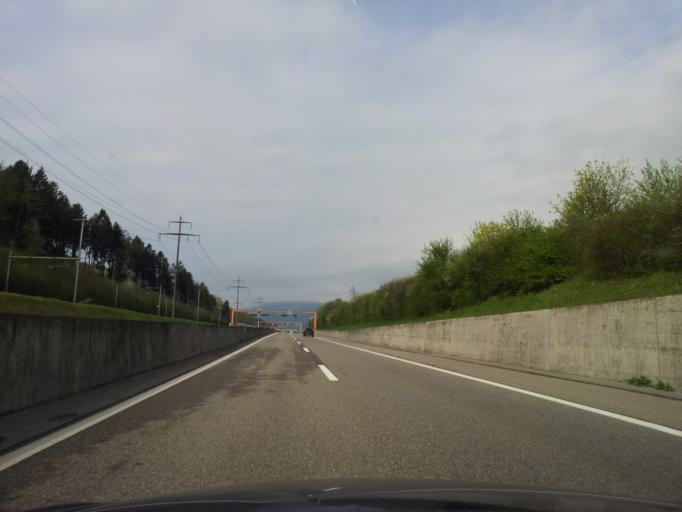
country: CH
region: Bern
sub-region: Biel/Bienne District
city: Pieterlen
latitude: 47.1688
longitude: 7.3279
